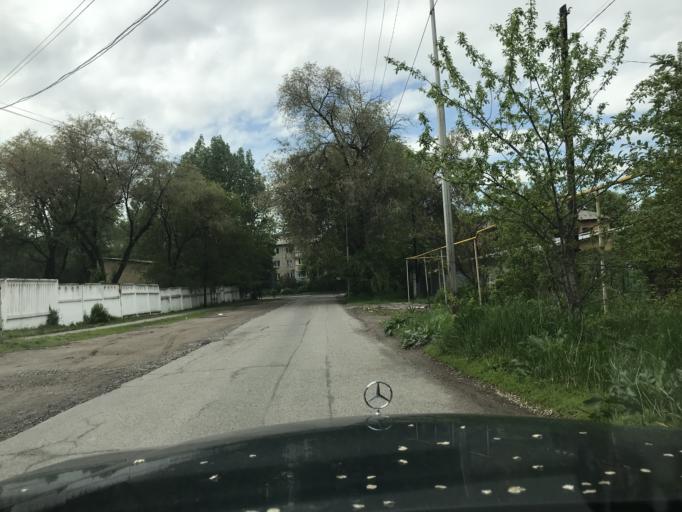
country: KZ
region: Almaty Qalasy
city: Almaty
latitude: 43.2076
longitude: 76.8696
